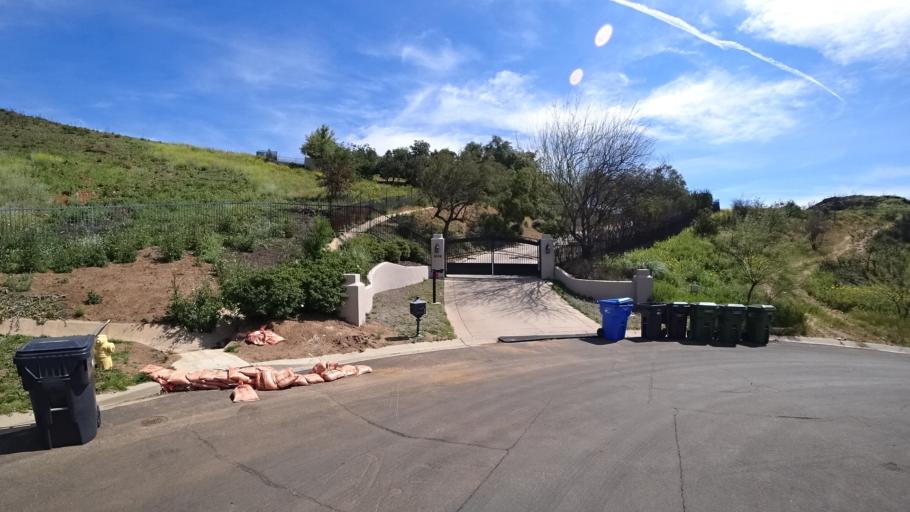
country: US
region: California
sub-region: Ventura County
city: Oak Park
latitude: 34.1945
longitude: -118.7993
